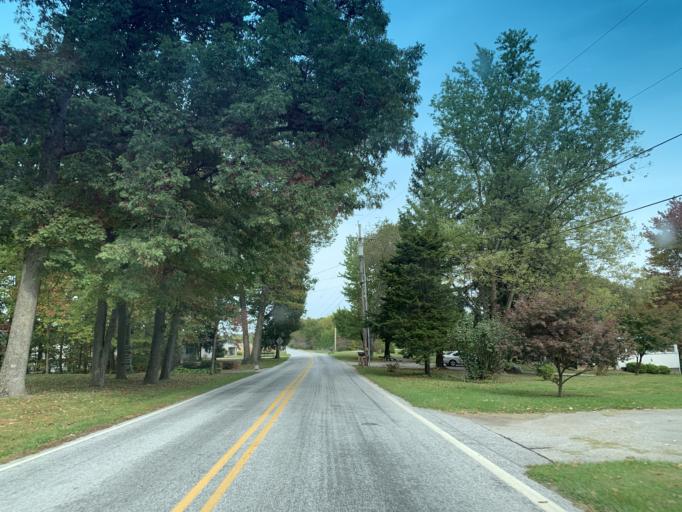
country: US
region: Pennsylvania
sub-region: York County
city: Windsor
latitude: 39.8724
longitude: -76.5131
